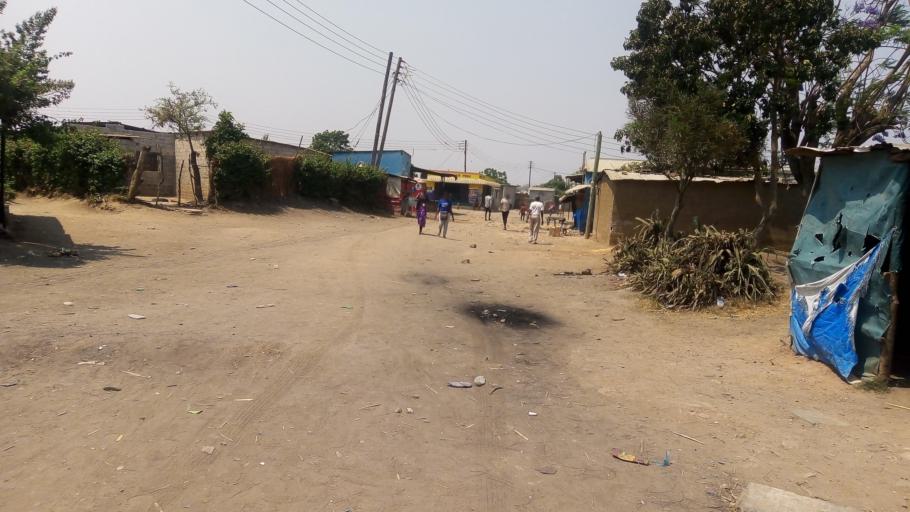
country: ZM
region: Lusaka
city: Lusaka
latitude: -15.4424
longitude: 28.3787
